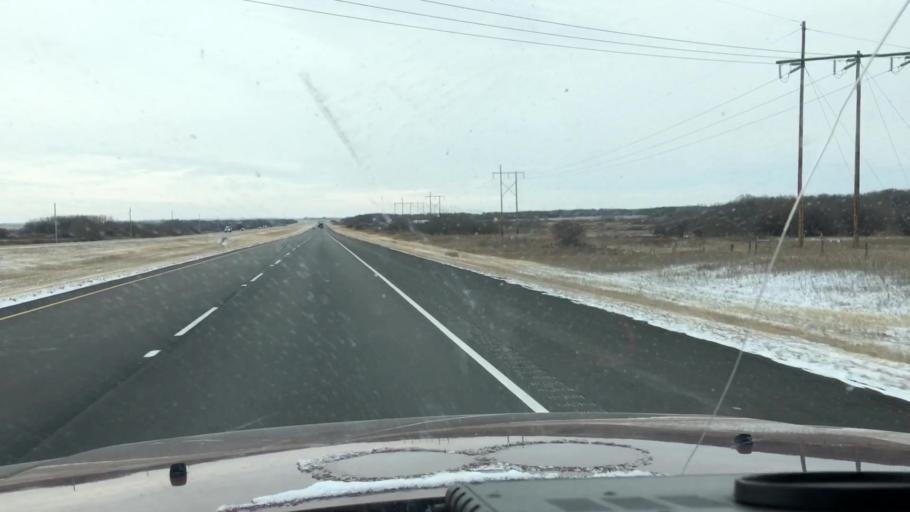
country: CA
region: Saskatchewan
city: Saskatoon
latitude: 51.8915
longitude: -106.5174
